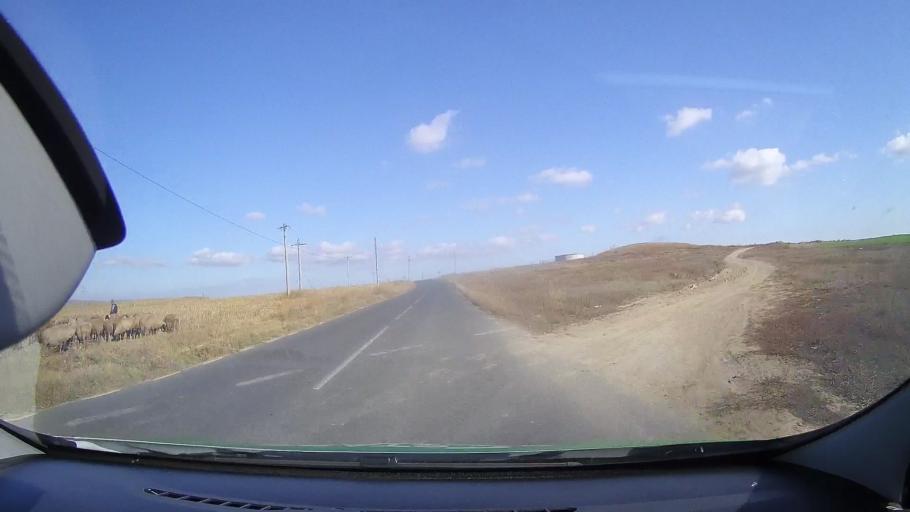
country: RO
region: Tulcea
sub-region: Comuna Ceamurlia de Jos
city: Ceamurlia de Jos
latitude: 44.7404
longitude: 28.6940
